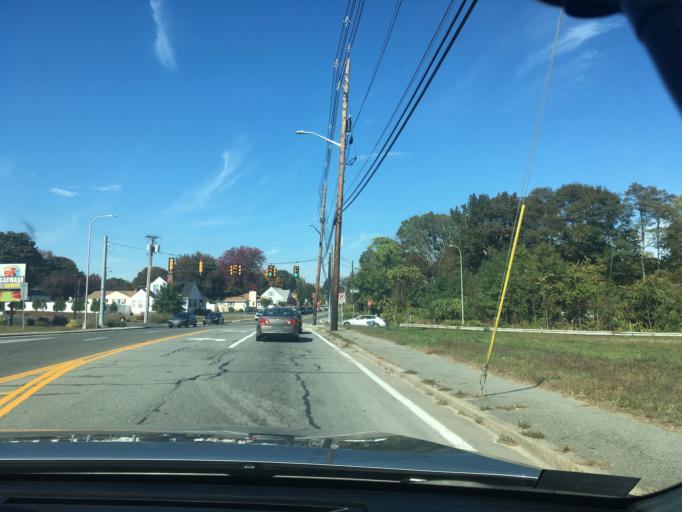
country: US
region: Rhode Island
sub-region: Providence County
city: North Providence
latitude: 41.8226
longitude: -71.4705
